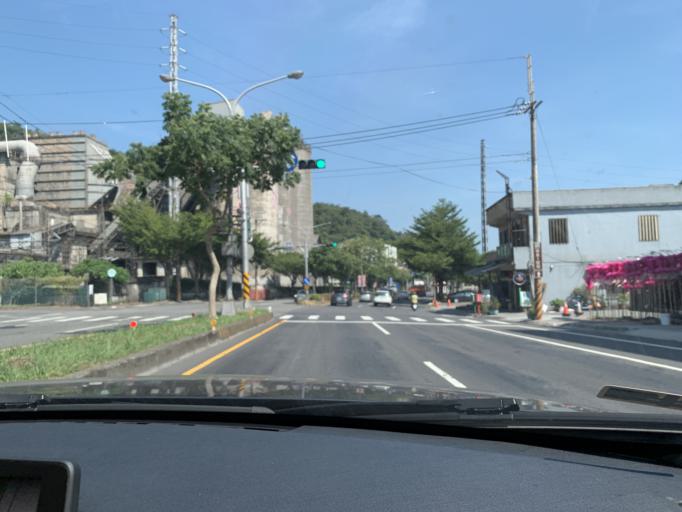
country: TW
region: Taiwan
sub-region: Yilan
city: Yilan
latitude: 24.6078
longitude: 121.8273
